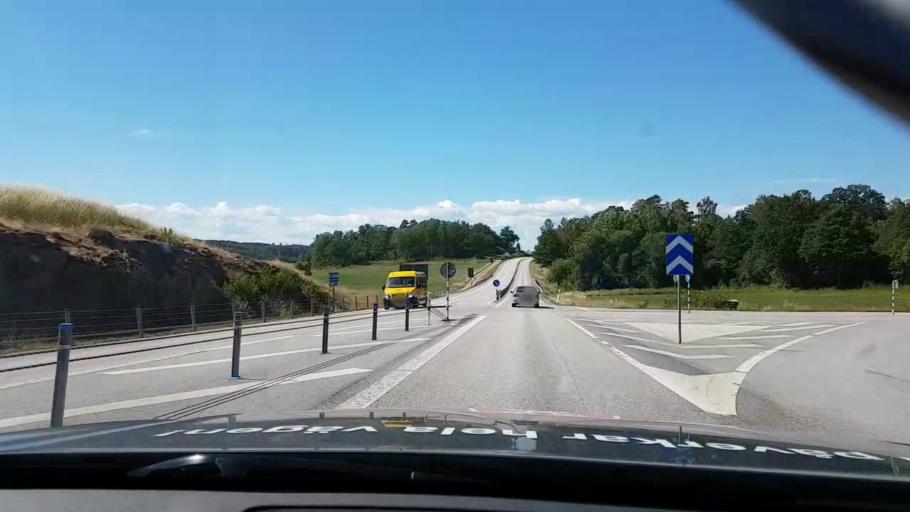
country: SE
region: Kalmar
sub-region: Vasterviks Kommun
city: Gamleby
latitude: 57.8709
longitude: 16.4103
